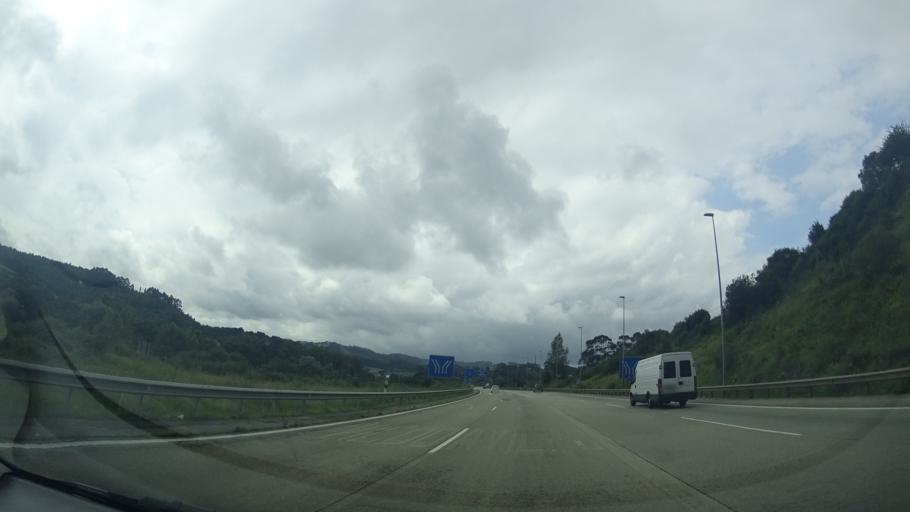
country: ES
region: Asturias
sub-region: Province of Asturias
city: Corvera de Asturias
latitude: 43.5025
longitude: -5.7760
